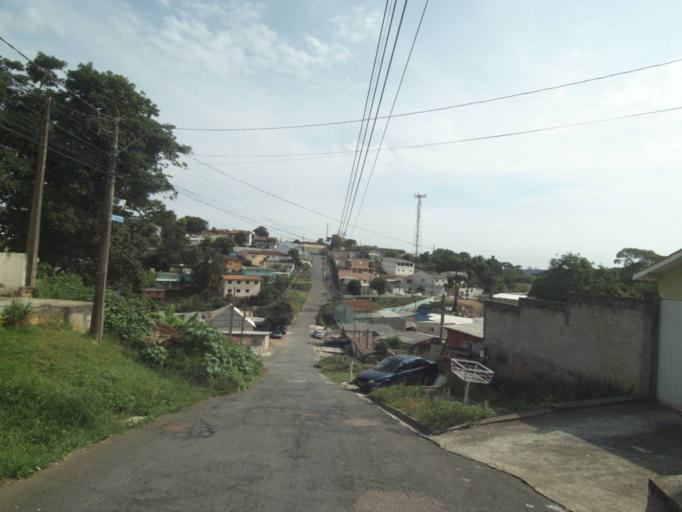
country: BR
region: Parana
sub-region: Curitiba
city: Curitiba
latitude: -25.4089
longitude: -49.3019
